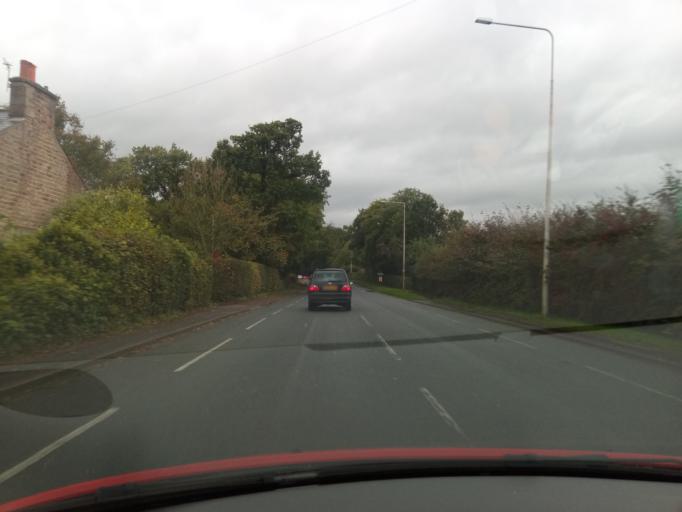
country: GB
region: England
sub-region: Lancashire
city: Catterall
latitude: 53.8394
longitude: -2.7399
